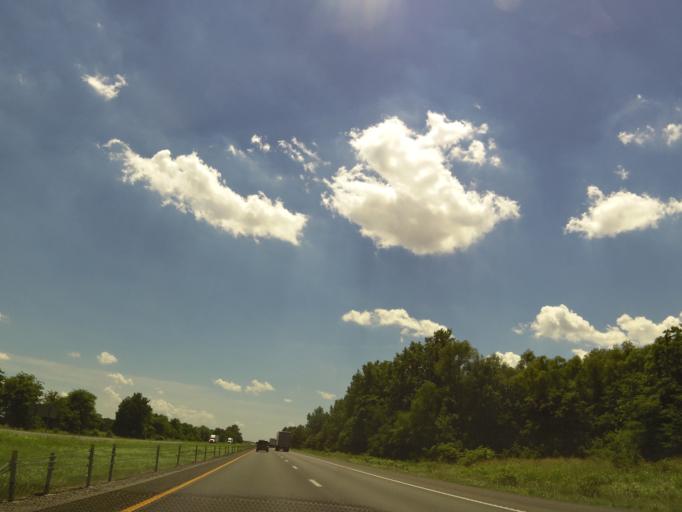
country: US
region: Missouri
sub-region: New Madrid County
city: Portageville
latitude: 36.4173
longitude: -89.6886
